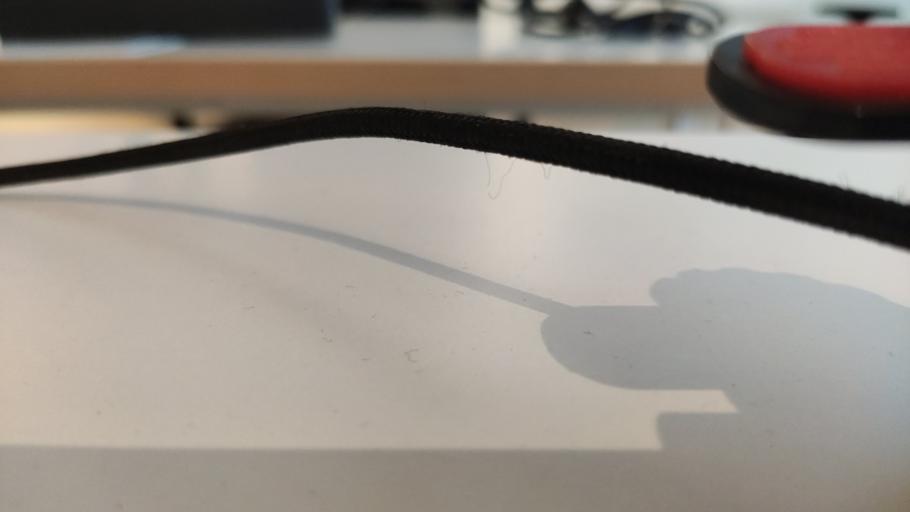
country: RU
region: Moskovskaya
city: Novopetrovskoye
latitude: 55.9155
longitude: 36.4400
